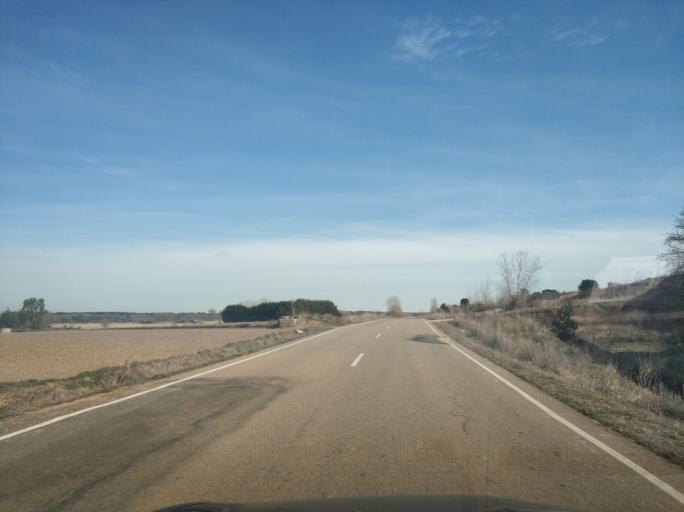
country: ES
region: Castille and Leon
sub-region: Provincia de Salamanca
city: Valverdon
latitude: 41.0382
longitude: -5.7847
